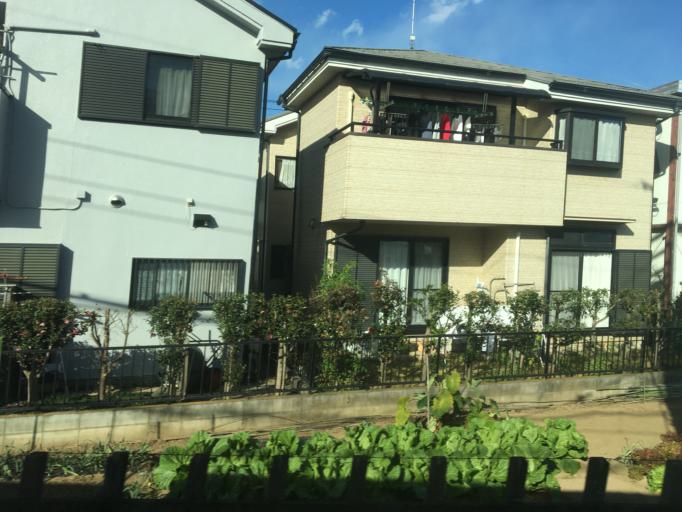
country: JP
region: Saitama
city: Kumagaya
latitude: 36.0475
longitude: 139.3620
